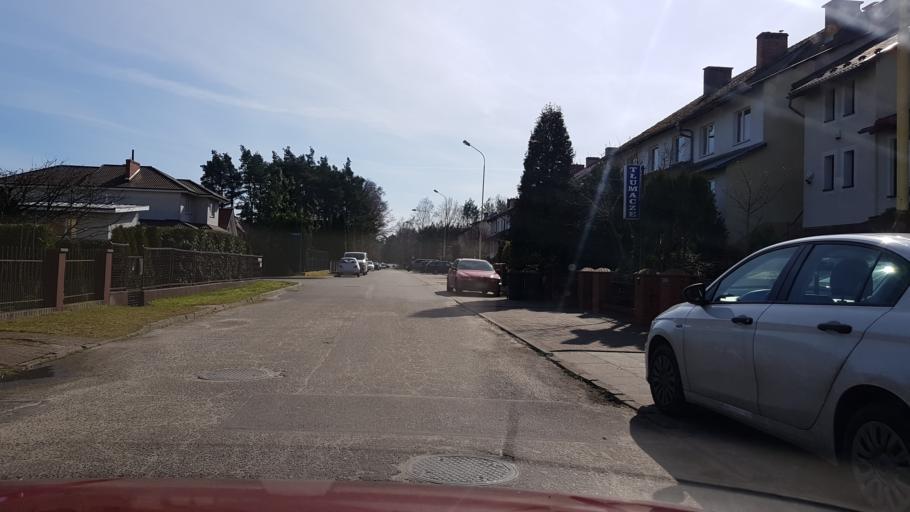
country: PL
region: West Pomeranian Voivodeship
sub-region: Powiat goleniowski
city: Goleniow
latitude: 53.5536
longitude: 14.8306
